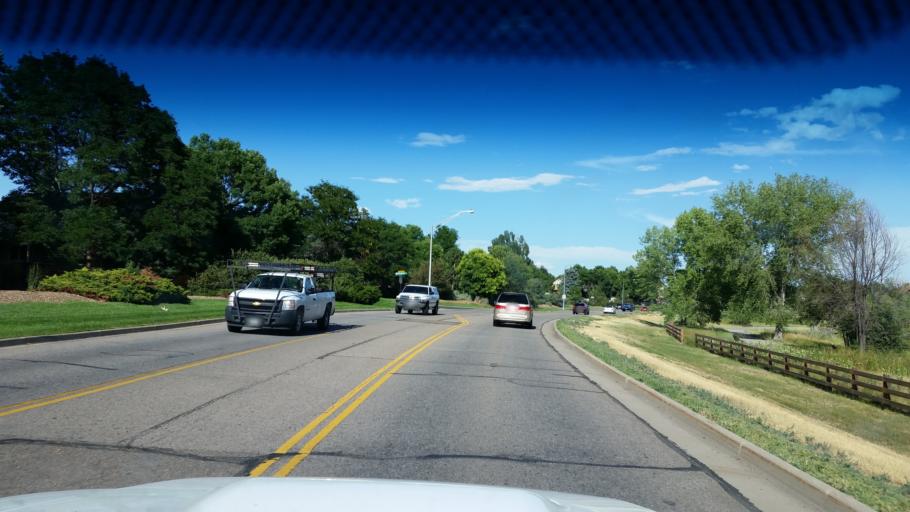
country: US
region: Colorado
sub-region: Adams County
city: Northglenn
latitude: 39.9289
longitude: -104.9533
